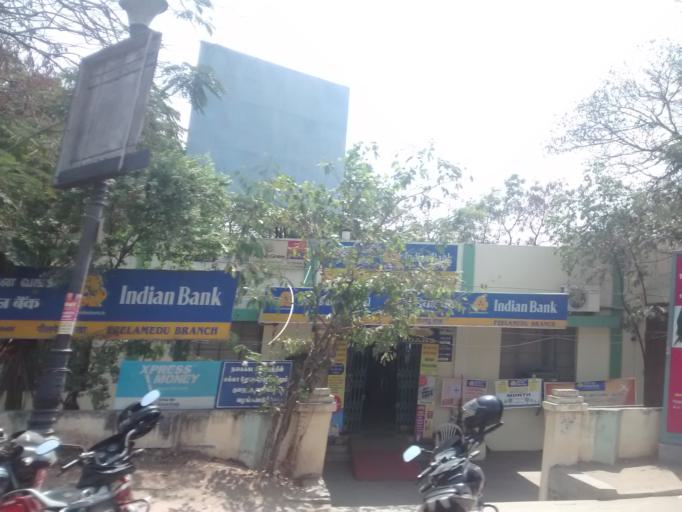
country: IN
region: Tamil Nadu
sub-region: Coimbatore
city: Singanallur
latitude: 11.0286
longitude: 77.0255
